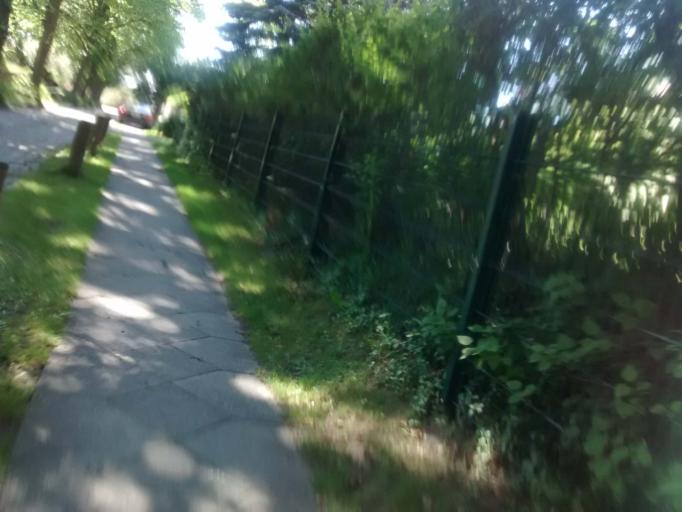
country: DE
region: Brandenburg
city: Hohen Neuendorf
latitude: 52.6776
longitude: 13.2730
